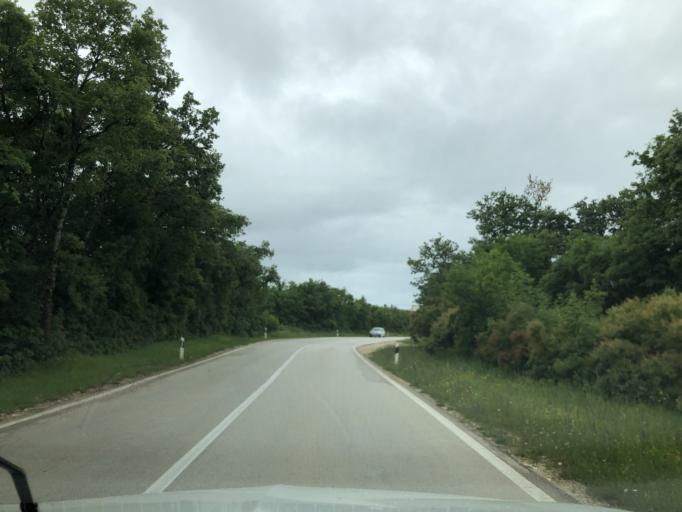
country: SI
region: Piran-Pirano
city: Seca
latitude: 45.4576
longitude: 13.6101
